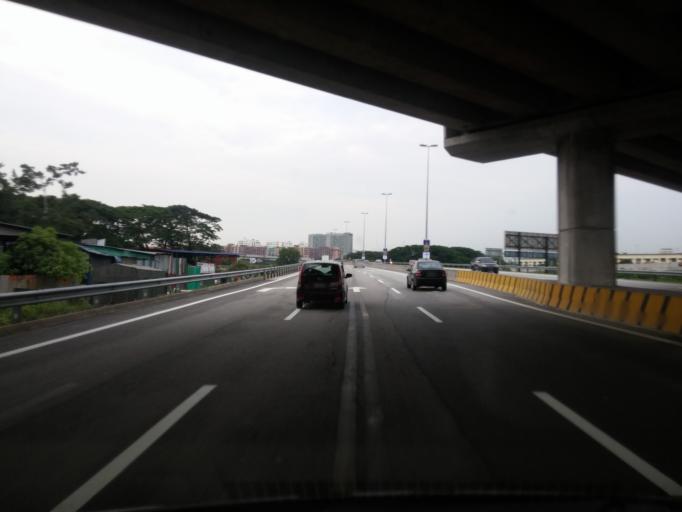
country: MY
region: Kuala Lumpur
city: Kuala Lumpur
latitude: 3.1141
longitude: 101.7148
